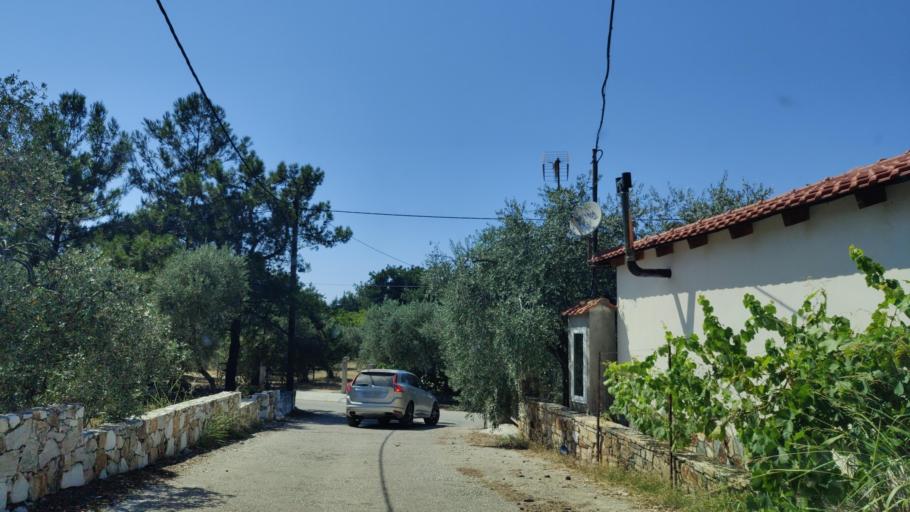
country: GR
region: East Macedonia and Thrace
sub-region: Nomos Kavalas
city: Prinos
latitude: 40.7922
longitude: 24.6330
